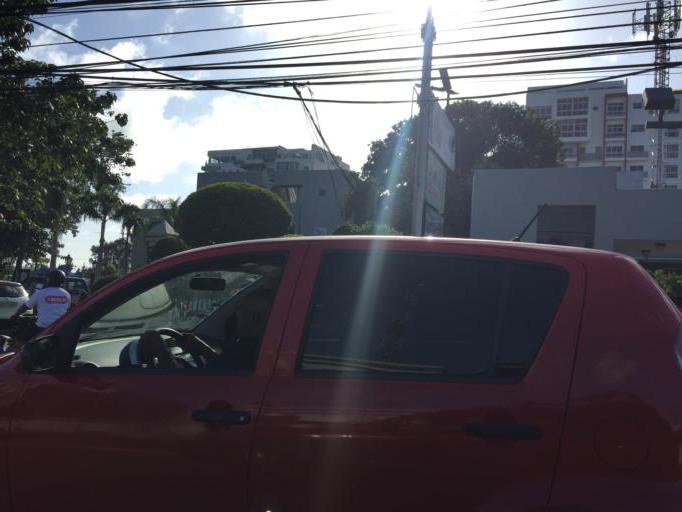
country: DO
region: Nacional
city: La Julia
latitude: 18.4600
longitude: -69.9272
